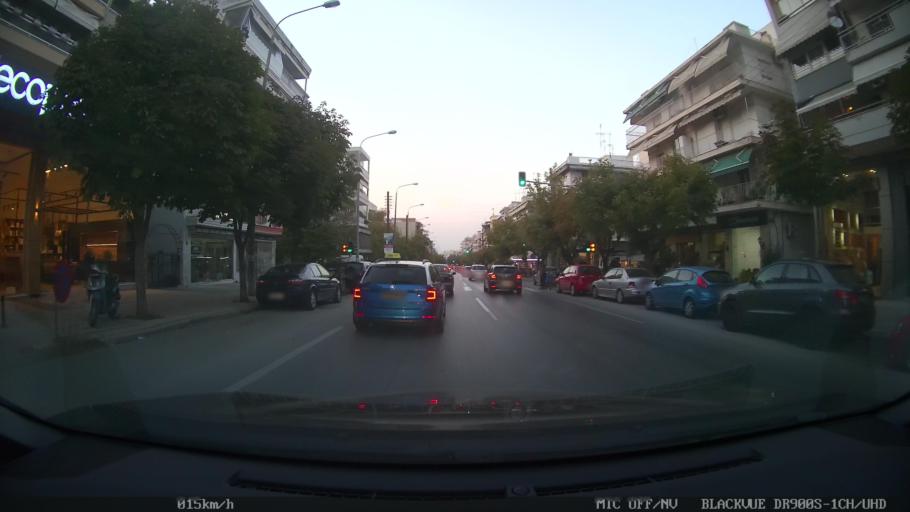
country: GR
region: Central Macedonia
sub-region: Nomos Thessalonikis
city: Kalamaria
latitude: 40.5831
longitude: 22.9650
